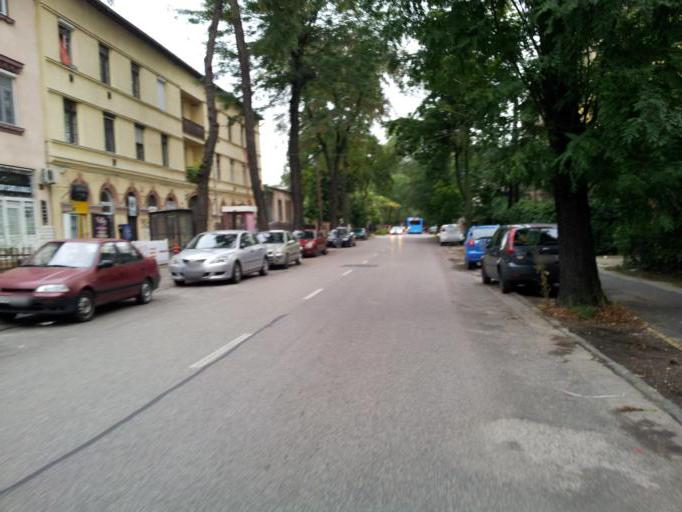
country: HU
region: Budapest
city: Budapest XIV. keruelet
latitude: 47.5209
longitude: 19.1108
